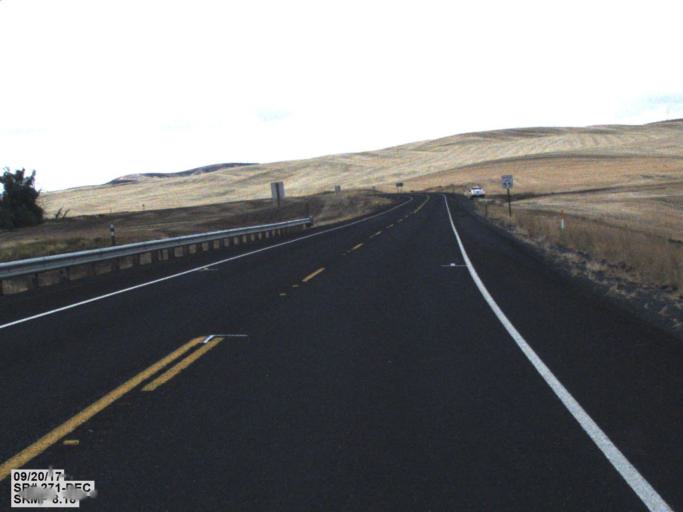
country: US
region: Washington
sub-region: Whitman County
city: Colfax
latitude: 47.2080
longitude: -117.3573
